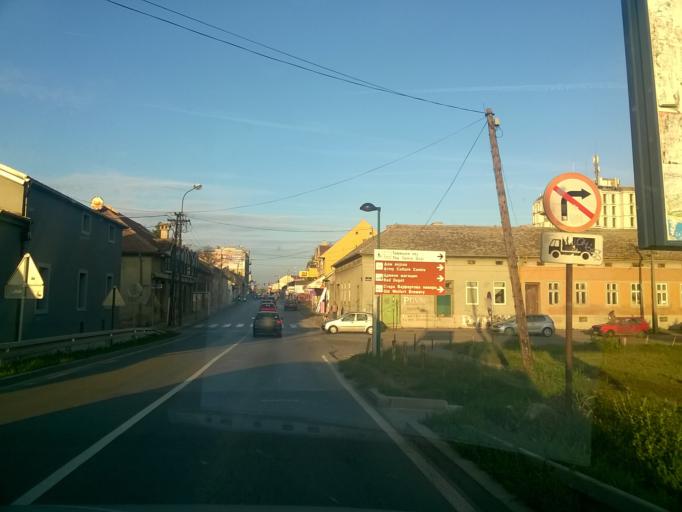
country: RS
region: Autonomna Pokrajina Vojvodina
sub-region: Juznobanatski Okrug
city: Pancevo
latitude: 44.8725
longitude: 20.6347
